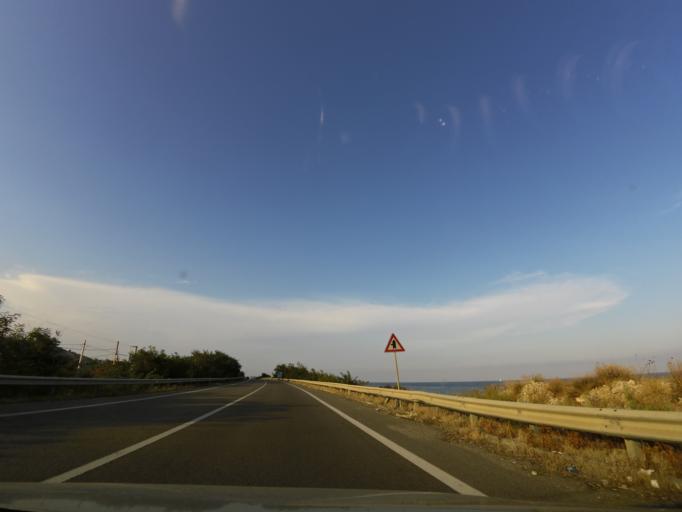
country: IT
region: Calabria
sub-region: Provincia di Reggio Calabria
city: Monasterace Marina
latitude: 38.4250
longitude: 16.5682
